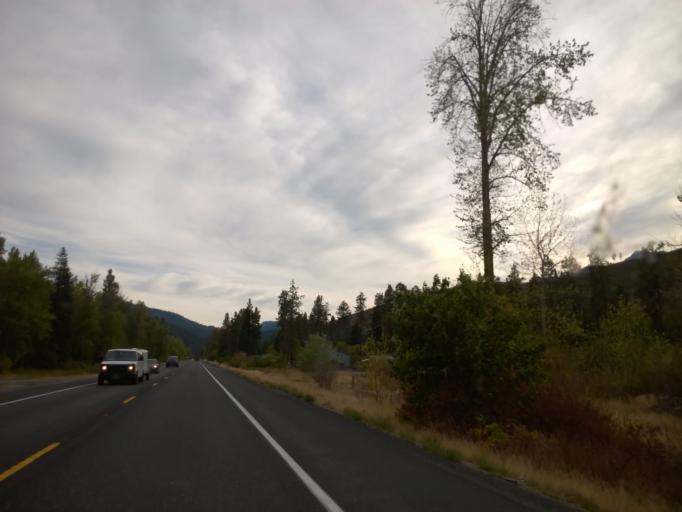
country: US
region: Washington
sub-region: Chelan County
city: Leavenworth
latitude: 47.5313
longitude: -120.6221
